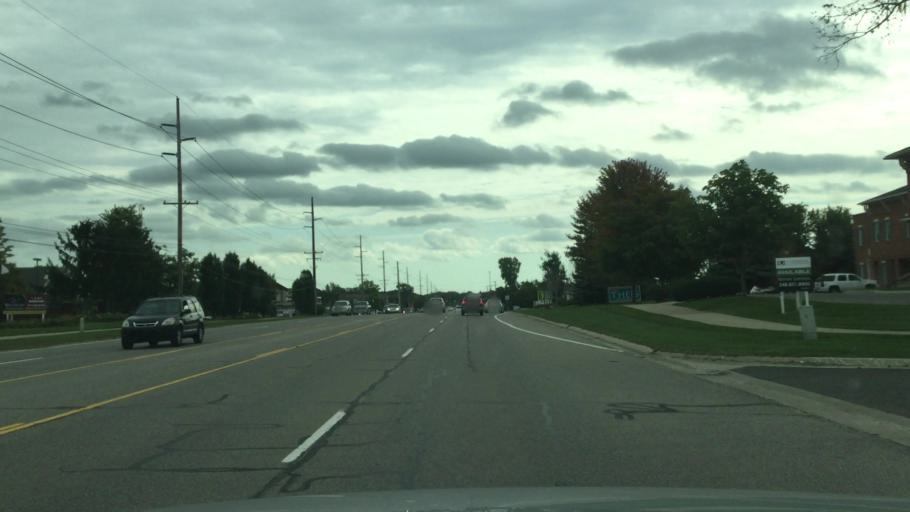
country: US
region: Michigan
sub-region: Livingston County
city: Howell
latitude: 42.5847
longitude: -83.8686
